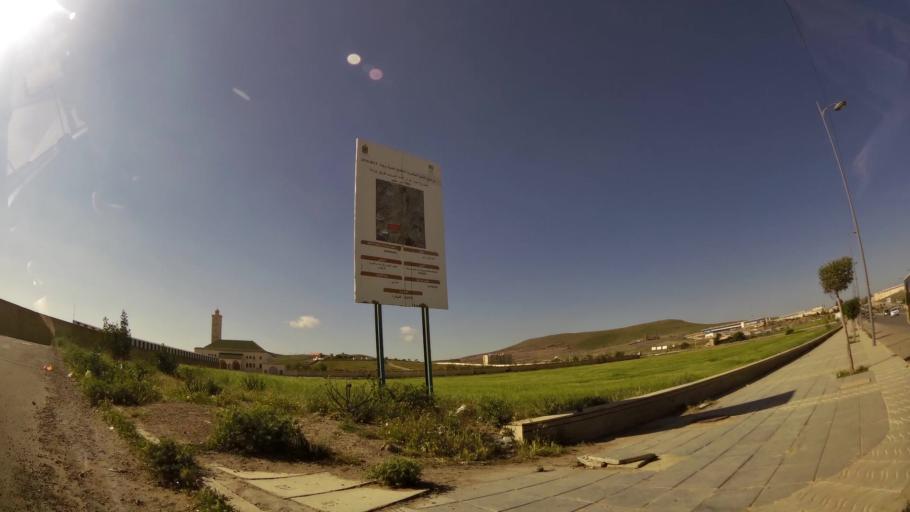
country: MA
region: Oriental
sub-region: Oujda-Angad
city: Oujda
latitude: 34.6569
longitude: -1.9547
